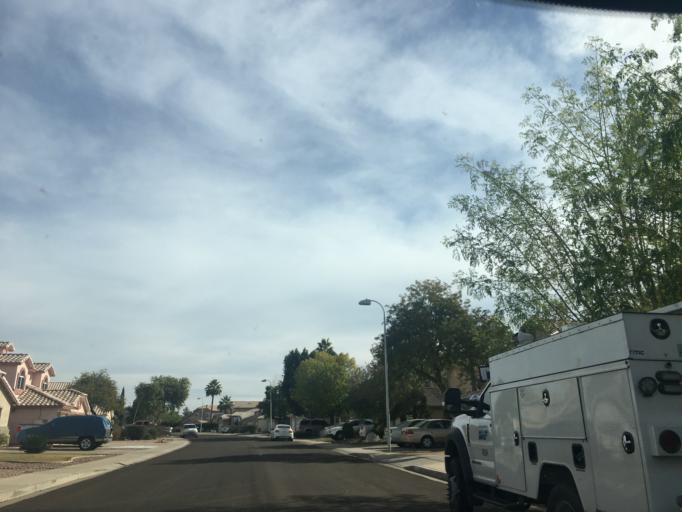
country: US
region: Arizona
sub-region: Maricopa County
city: Gilbert
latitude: 33.3463
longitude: -111.8096
